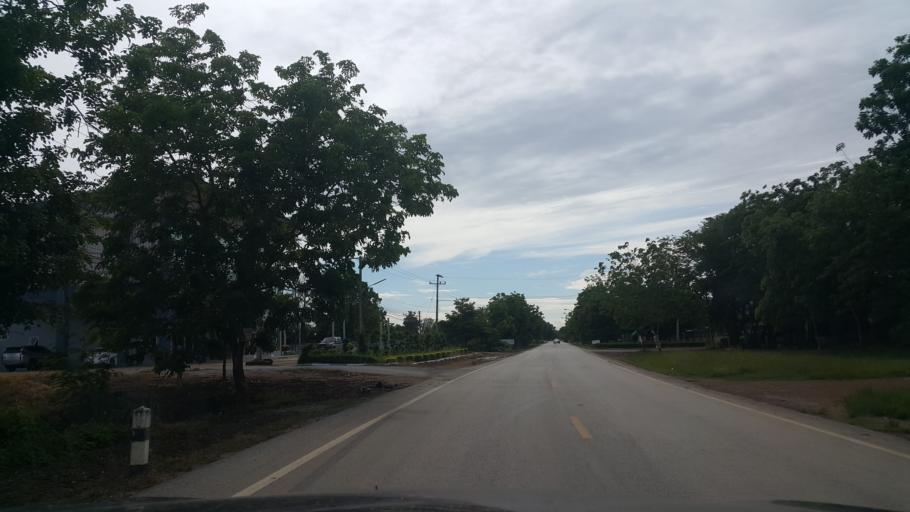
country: TH
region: Sukhothai
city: Si Nakhon
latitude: 17.2767
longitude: 99.9689
